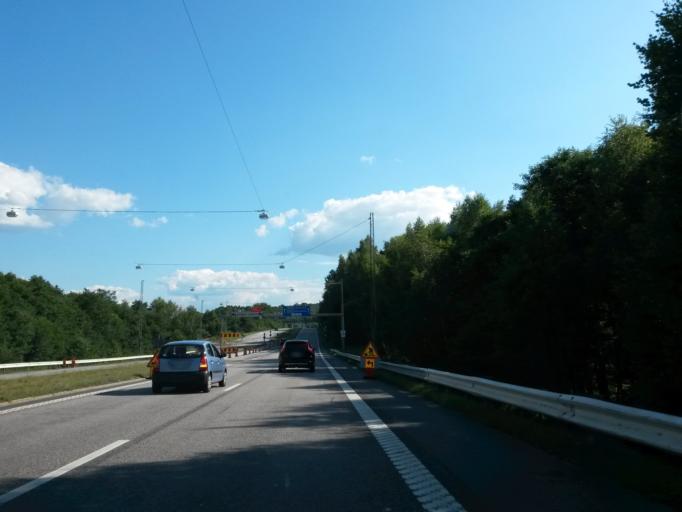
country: SE
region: Vaestra Goetaland
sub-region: Goteborg
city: Gardsten
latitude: 57.7962
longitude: 12.0422
